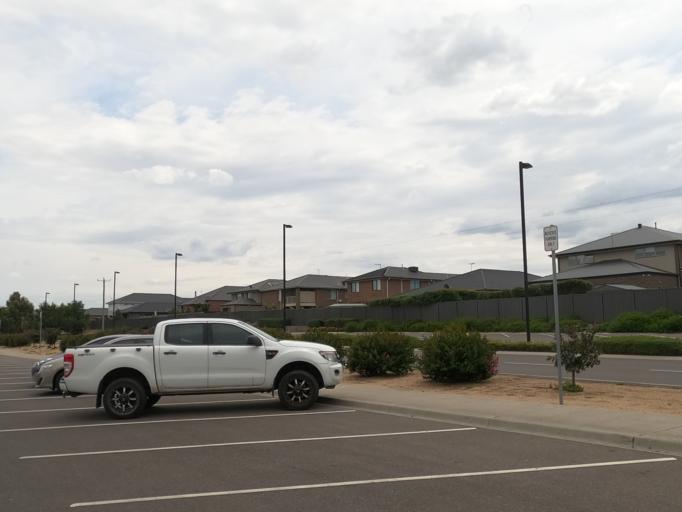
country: AU
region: Victoria
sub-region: Hume
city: Greenvale
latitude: -37.6273
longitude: 144.8888
